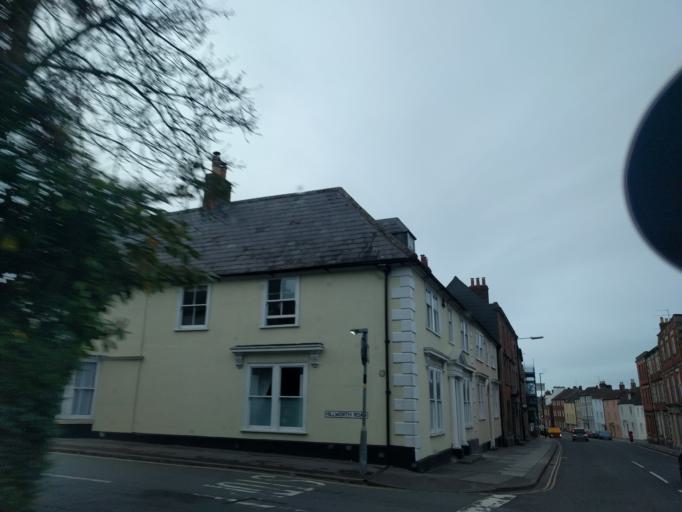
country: GB
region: England
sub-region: Wiltshire
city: Devizes
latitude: 51.3486
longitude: -1.9926
